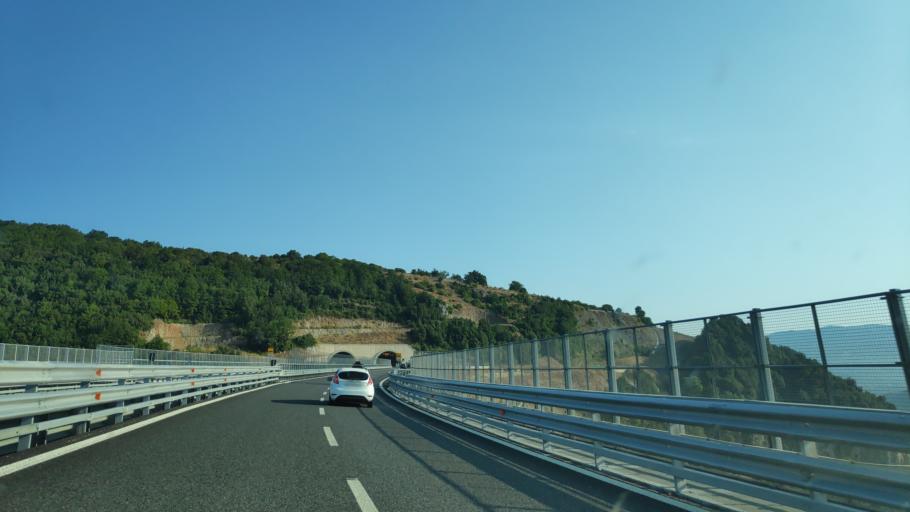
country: IT
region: Calabria
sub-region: Provincia di Cosenza
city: Laino Castello-Nuovo Centro
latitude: 39.9403
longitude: 15.9592
